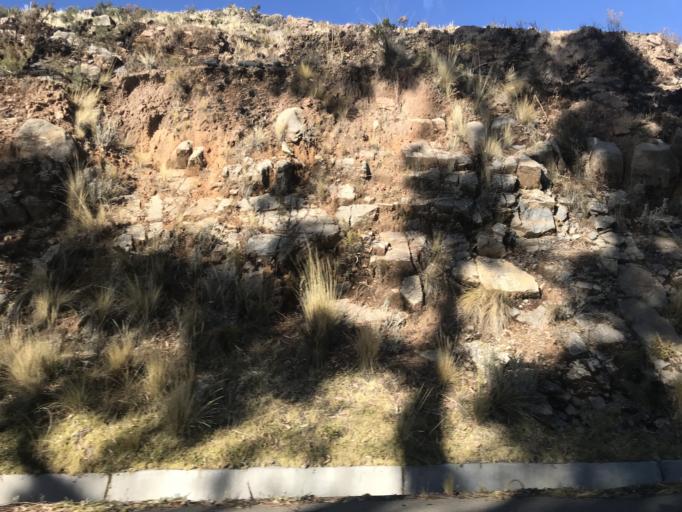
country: BO
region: La Paz
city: San Pedro
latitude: -16.1903
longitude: -68.9242
